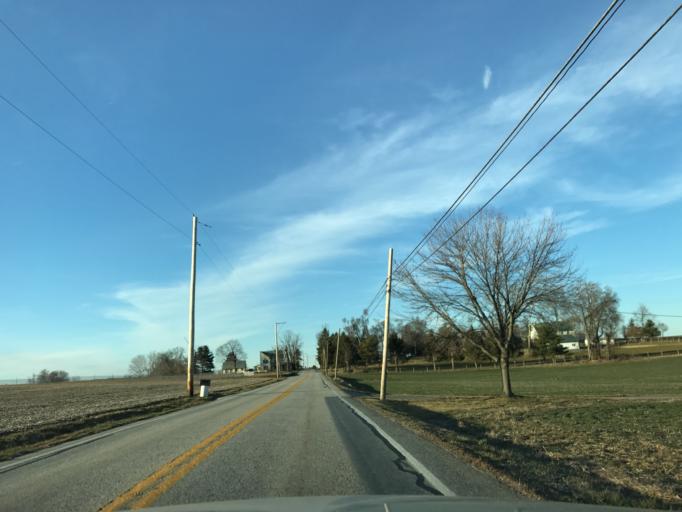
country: US
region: Pennsylvania
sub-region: Lancaster County
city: Maytown
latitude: 40.0873
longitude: -76.5914
